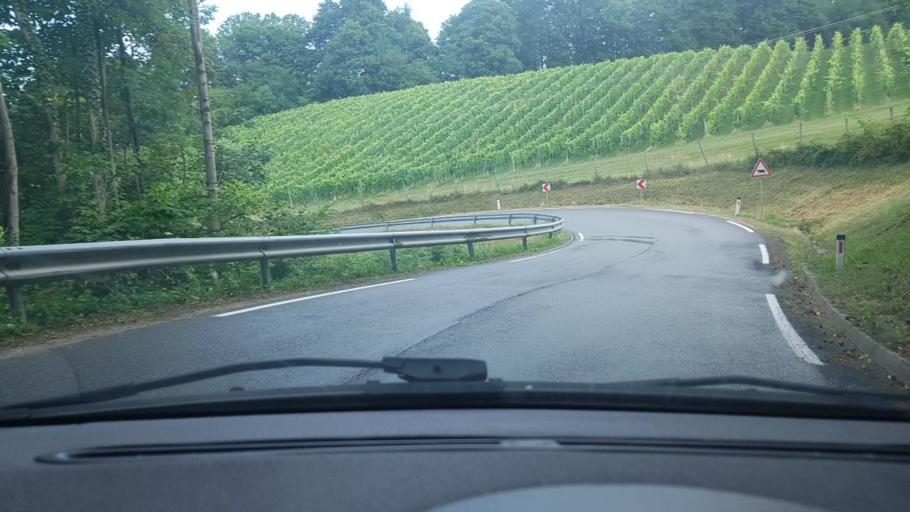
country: AT
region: Styria
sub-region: Politischer Bezirk Suedoststeiermark
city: Mureck
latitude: 46.6929
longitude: 15.7648
